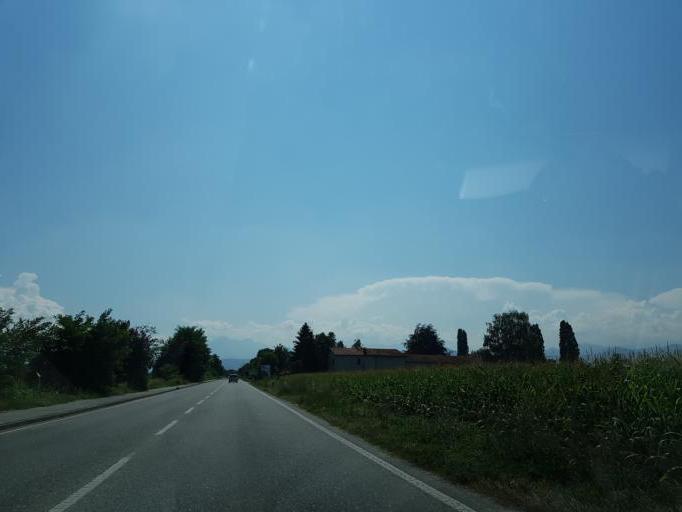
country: IT
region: Piedmont
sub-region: Provincia di Cuneo
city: Cuneo
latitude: 44.4033
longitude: 7.5446
